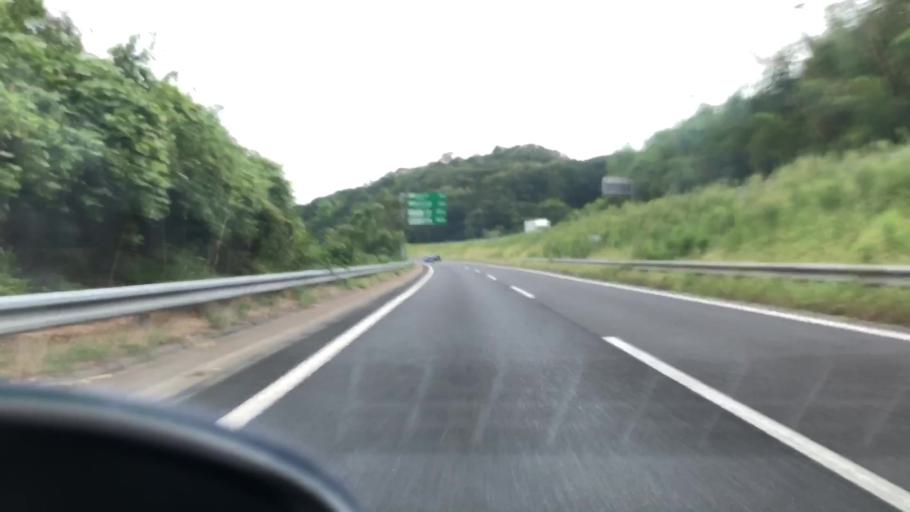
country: JP
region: Hyogo
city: Sandacho
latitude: 34.8901
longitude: 135.1294
